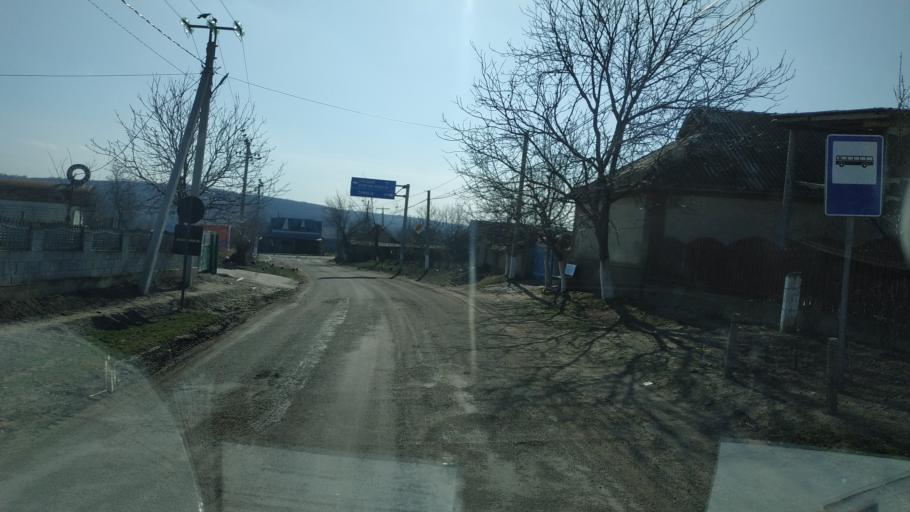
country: MD
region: Causeni
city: Causeni
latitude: 46.6000
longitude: 29.2557
